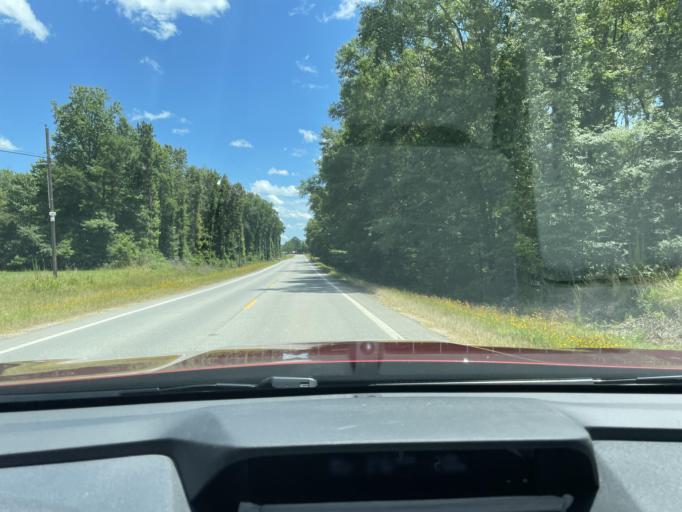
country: US
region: Arkansas
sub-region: Drew County
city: Monticello
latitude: 33.6094
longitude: -91.7384
